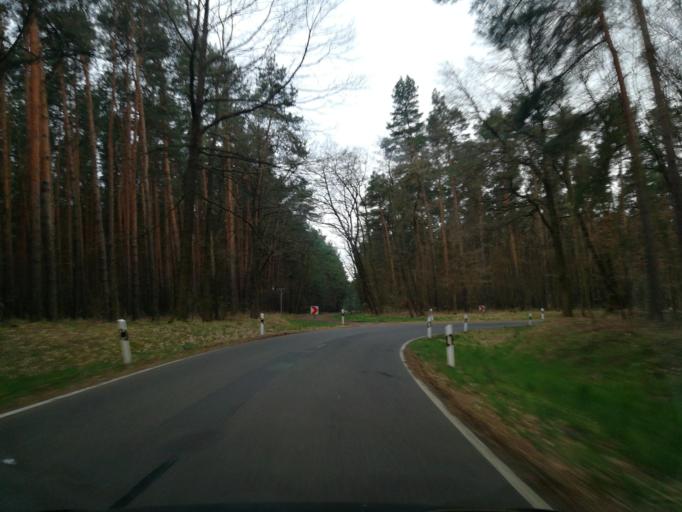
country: DE
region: Brandenburg
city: Vetschau
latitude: 51.7330
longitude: 14.1262
